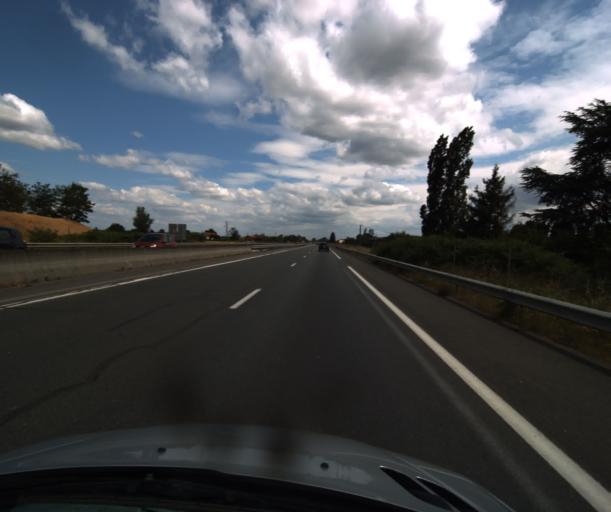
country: FR
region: Midi-Pyrenees
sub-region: Departement du Tarn-et-Garonne
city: Bressols
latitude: 43.9651
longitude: 1.3301
